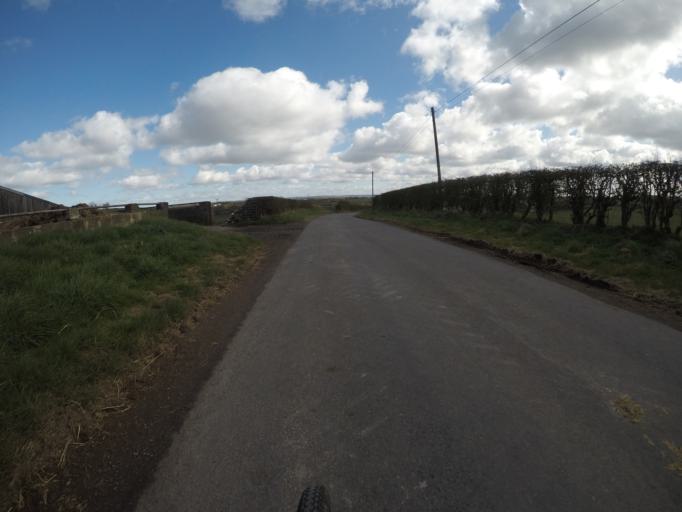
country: GB
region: Scotland
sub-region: North Ayrshire
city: Dreghorn
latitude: 55.5903
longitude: -4.5967
